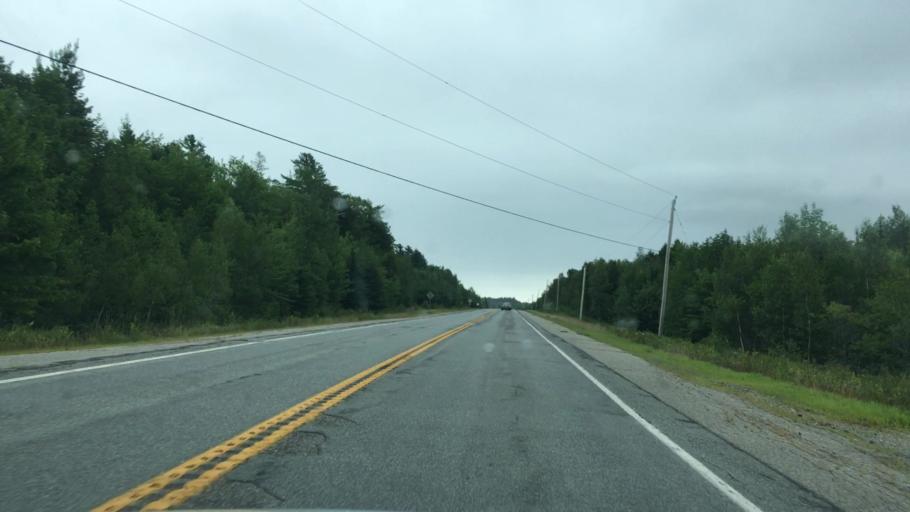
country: US
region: Maine
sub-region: Washington County
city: Cherryfield
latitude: 44.8560
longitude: -68.0529
